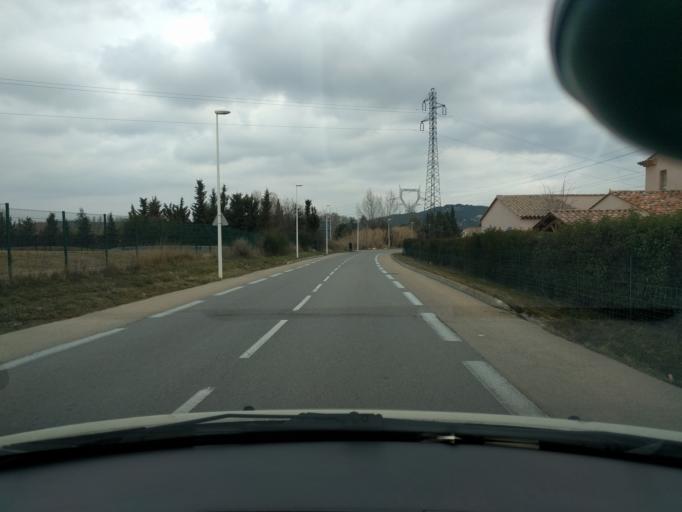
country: FR
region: Provence-Alpes-Cote d'Azur
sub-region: Departement des Bouches-du-Rhone
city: Bouc-Bel-Air
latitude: 43.4325
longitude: 5.4035
